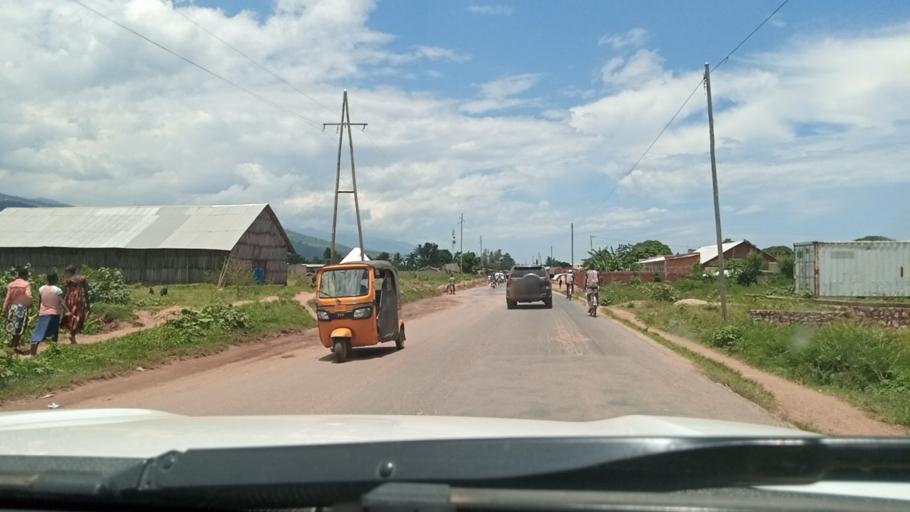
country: BI
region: Bujumbura Mairie
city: Bujumbura
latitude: -3.4659
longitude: 29.3499
